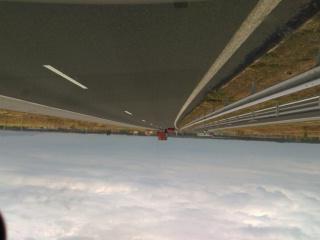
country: BG
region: Yambol
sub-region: Obshtina Yambol
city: Yambol
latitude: 42.5393
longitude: 26.4735
